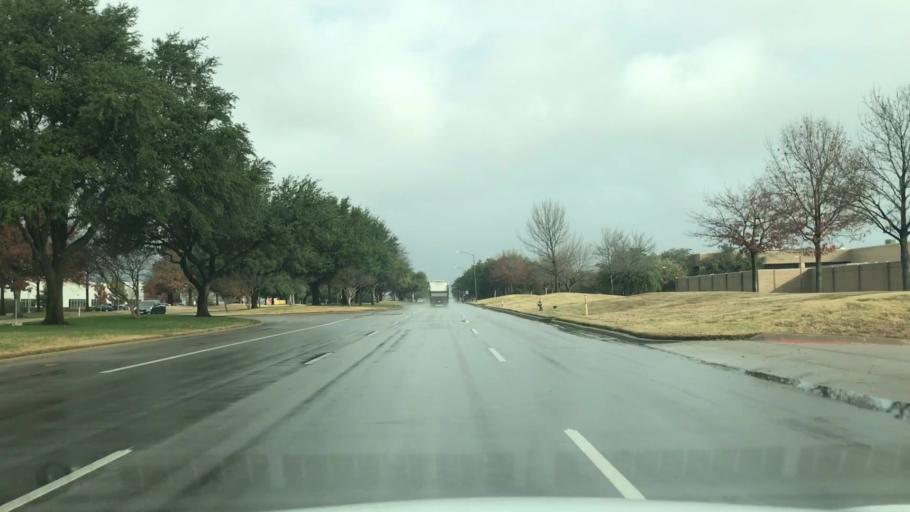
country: US
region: Texas
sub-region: Tarrant County
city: Euless
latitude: 32.8310
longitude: -97.0489
